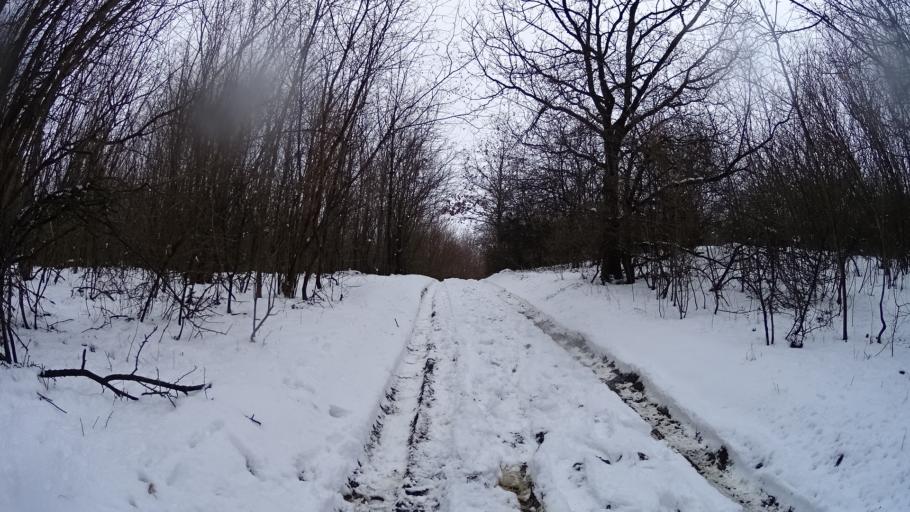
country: AT
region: Lower Austria
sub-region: Politischer Bezirk Korneuburg
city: Niederhollabrunn
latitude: 48.4225
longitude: 16.2737
